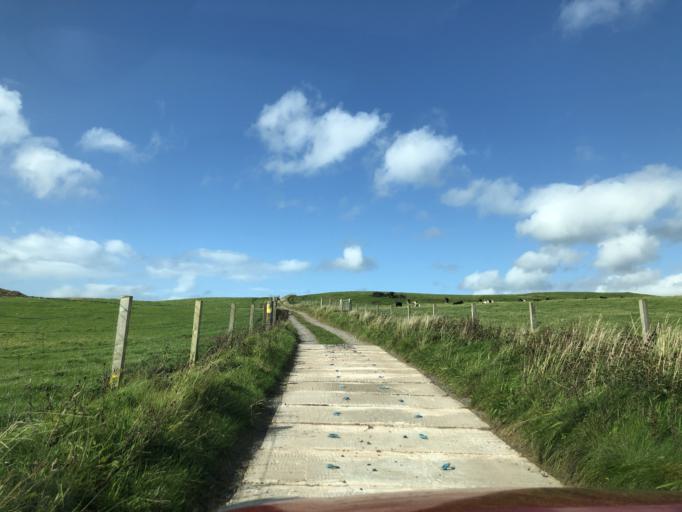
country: GB
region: Scotland
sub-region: Argyll and Bute
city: Campbeltown
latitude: 55.3116
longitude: -5.6068
